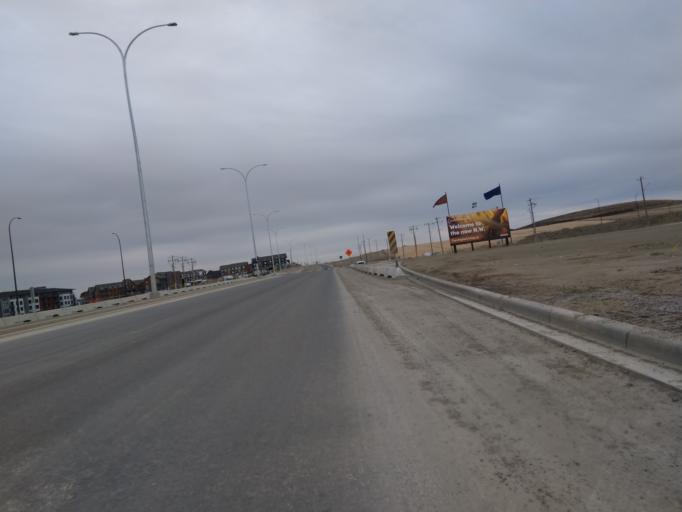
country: CA
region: Alberta
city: Airdrie
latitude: 51.1832
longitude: -114.0728
